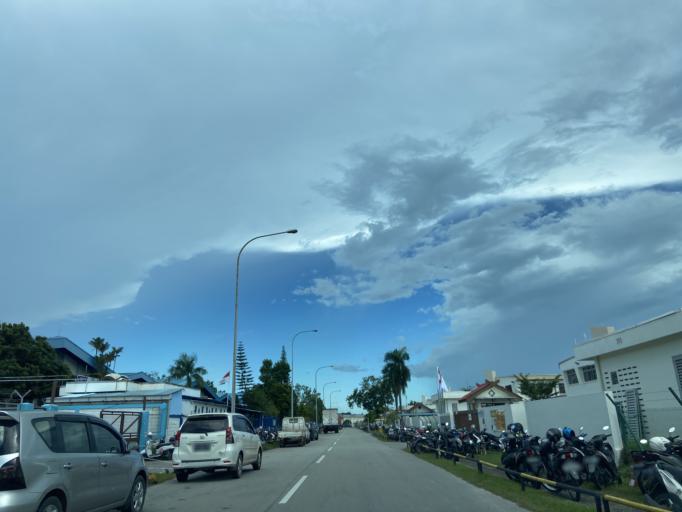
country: SG
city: Singapore
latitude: 1.0635
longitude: 104.0284
